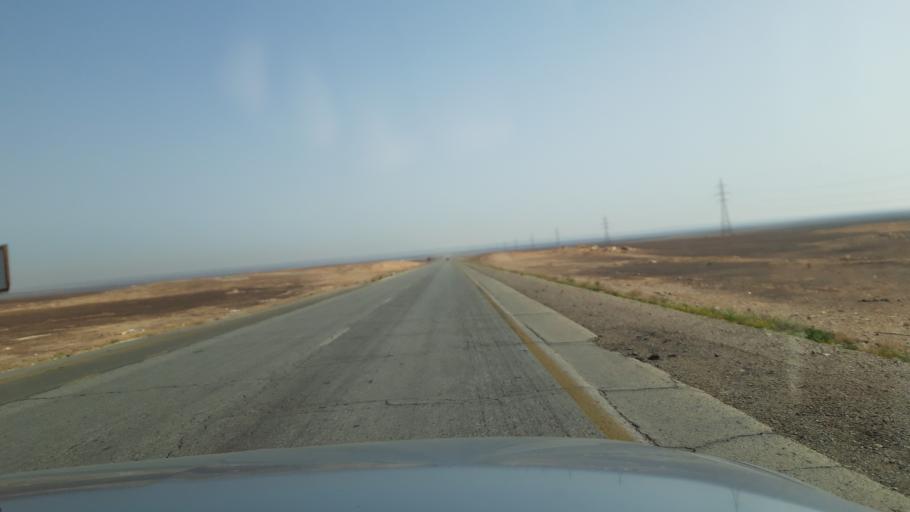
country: JO
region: Amman
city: Al Azraq ash Shamali
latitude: 31.7530
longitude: 36.5448
